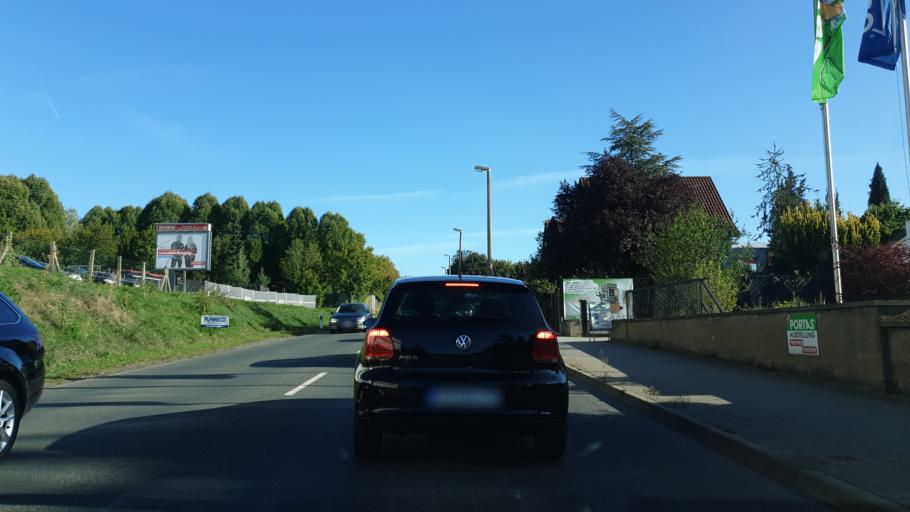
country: DE
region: Thuringia
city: Gera
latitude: 50.9172
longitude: 12.0557
